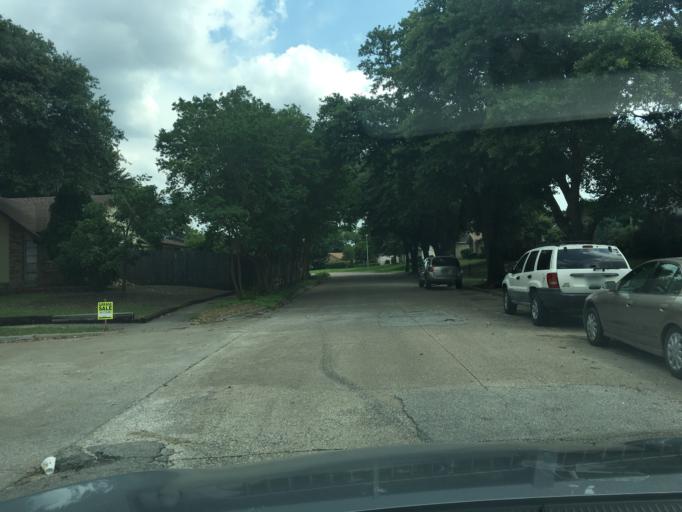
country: US
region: Texas
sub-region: Dallas County
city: Richardson
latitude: 32.9593
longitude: -96.6783
